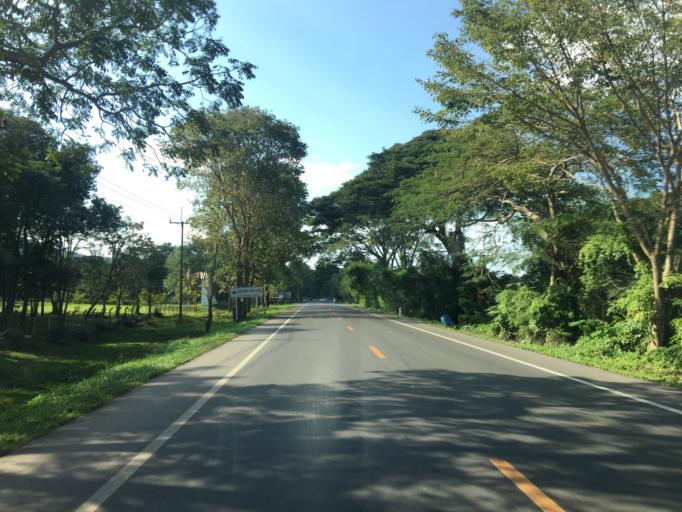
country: TH
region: Phayao
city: Chun
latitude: 19.3470
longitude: 100.1148
